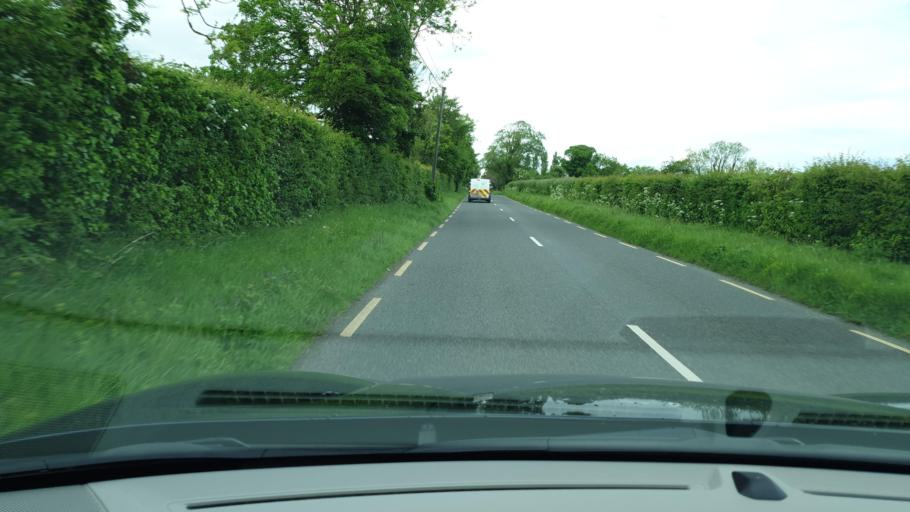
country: IE
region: Leinster
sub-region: An Mhi
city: Ratoath
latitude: 53.4880
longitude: -6.4346
